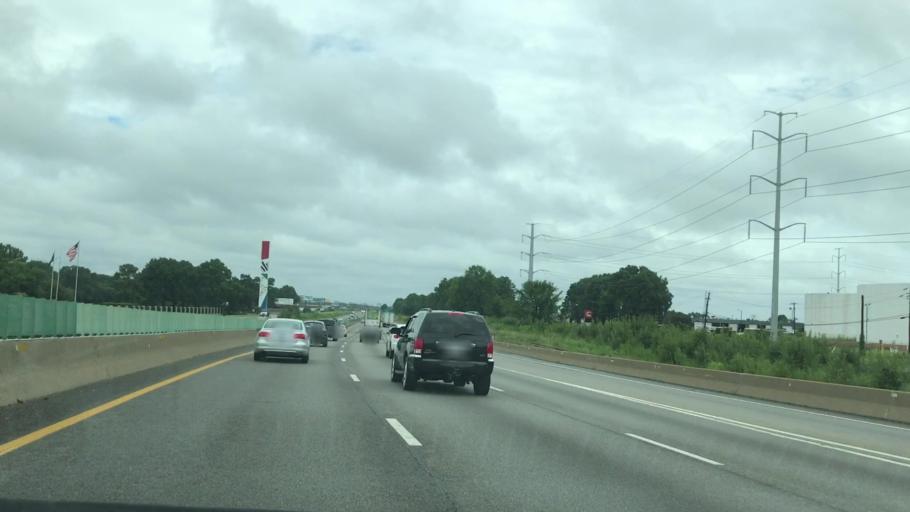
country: US
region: Virginia
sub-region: Chesterfield County
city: Bensley
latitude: 37.4697
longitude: -77.4282
